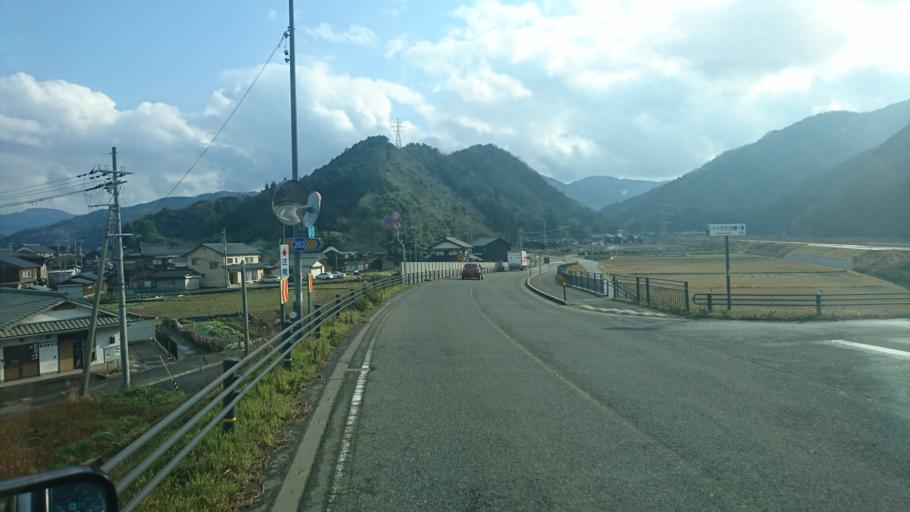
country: JP
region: Tottori
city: Tottori
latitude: 35.6083
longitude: 134.4704
